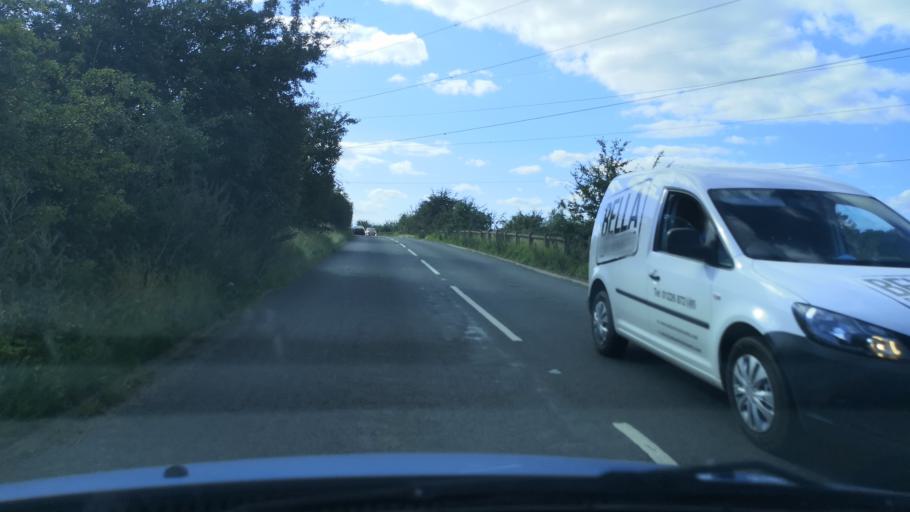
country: GB
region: England
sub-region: Doncaster
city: Kirk Sandall
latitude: 53.5723
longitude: -1.1001
